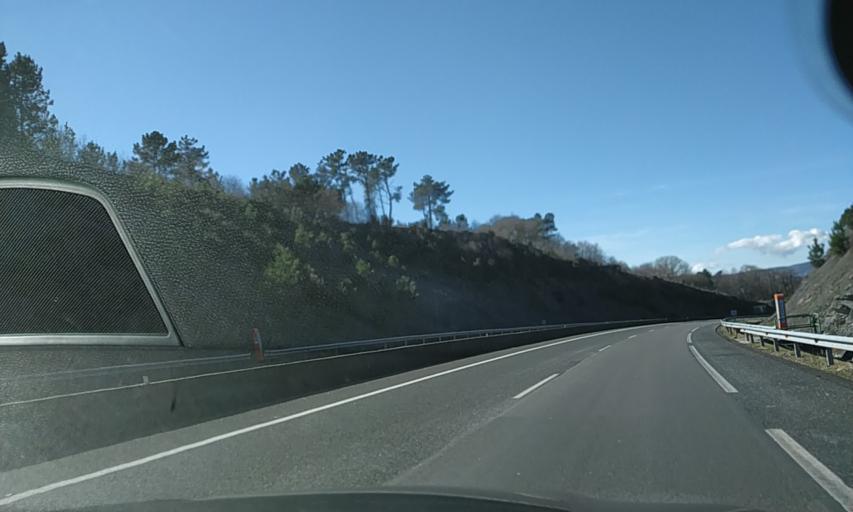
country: ES
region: Galicia
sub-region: Provincia de Pontevedra
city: Lalin
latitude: 42.6249
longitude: -8.1108
